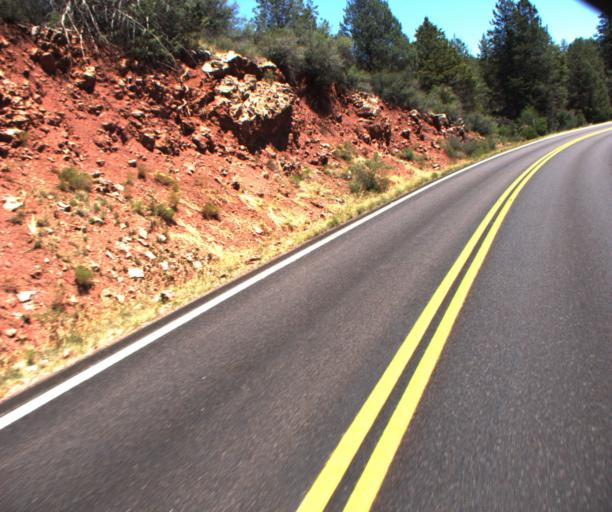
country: US
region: Arizona
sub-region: Gila County
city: Payson
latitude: 34.3145
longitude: -111.3699
